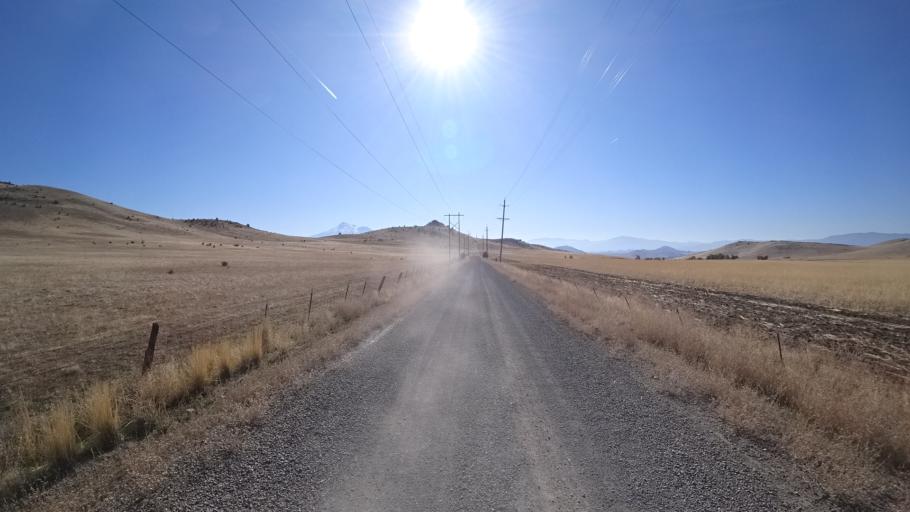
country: US
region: California
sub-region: Siskiyou County
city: Montague
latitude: 41.7522
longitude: -122.3594
